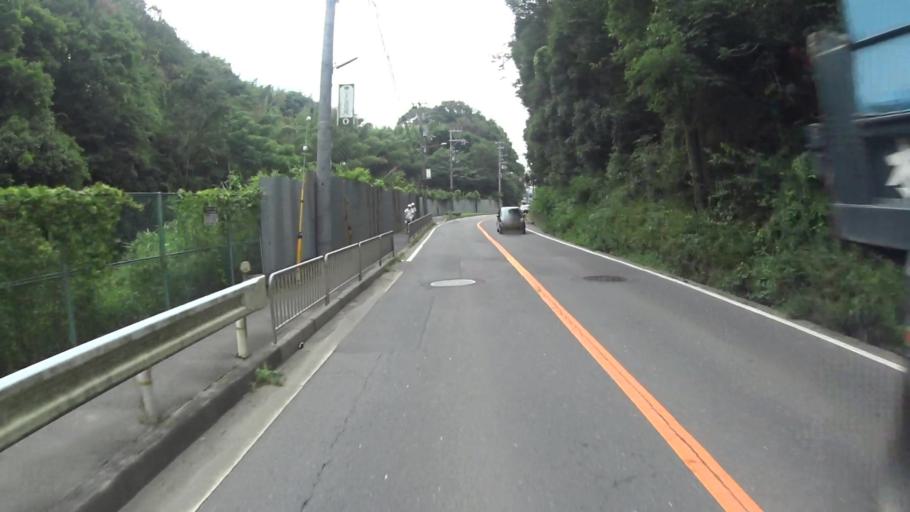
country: JP
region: Kyoto
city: Tanabe
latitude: 34.8080
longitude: 135.7231
